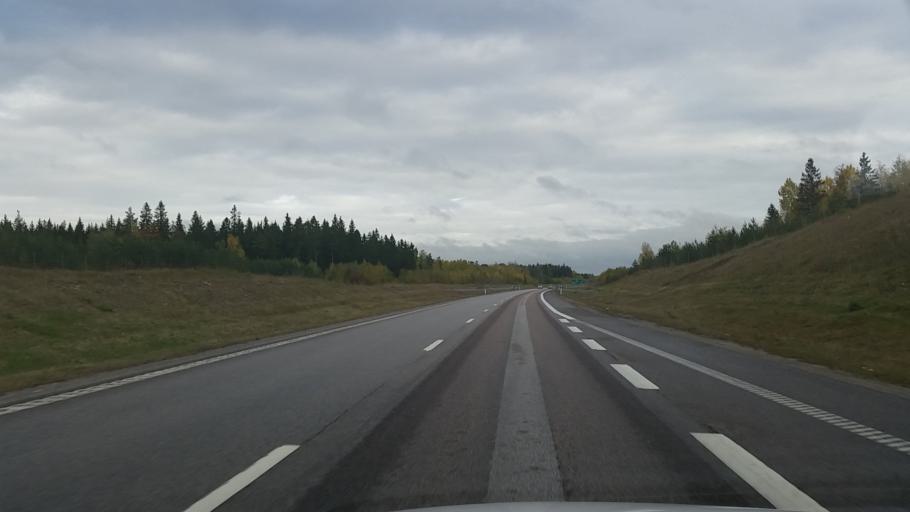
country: SE
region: Uppsala
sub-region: Osthammars Kommun
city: Bjorklinge
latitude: 60.0194
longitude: 17.6239
